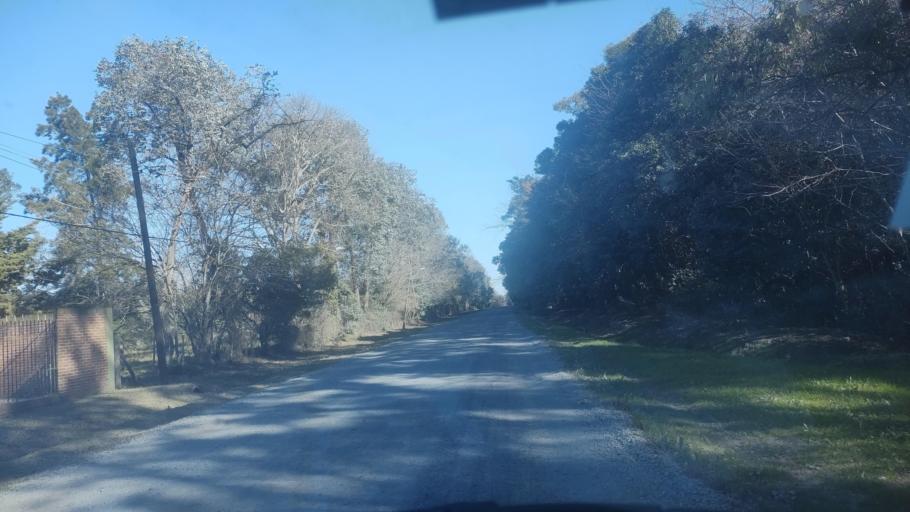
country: AR
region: Buenos Aires
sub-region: Partido de La Plata
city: La Plata
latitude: -34.8506
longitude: -58.1027
